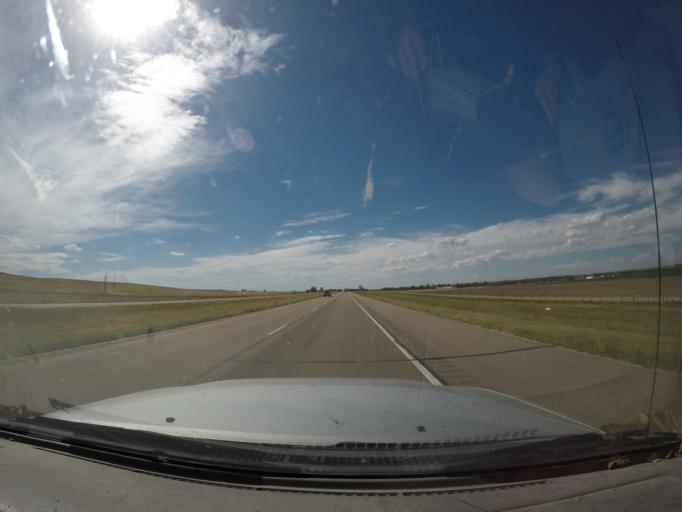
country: US
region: Nebraska
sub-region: Deuel County
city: Chappell
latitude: 41.0701
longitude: -102.4550
